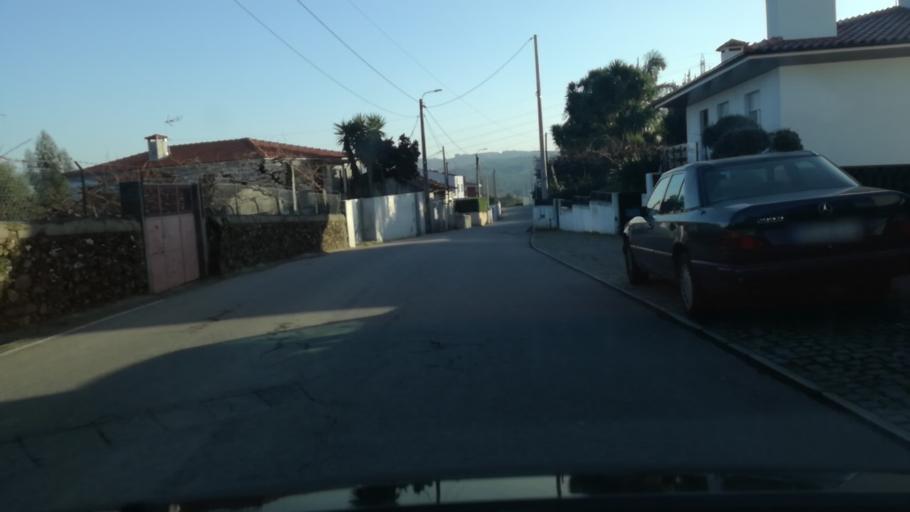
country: PT
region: Braga
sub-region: Vila Nova de Famalicao
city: Ferreiros
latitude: 41.3581
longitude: -8.5301
